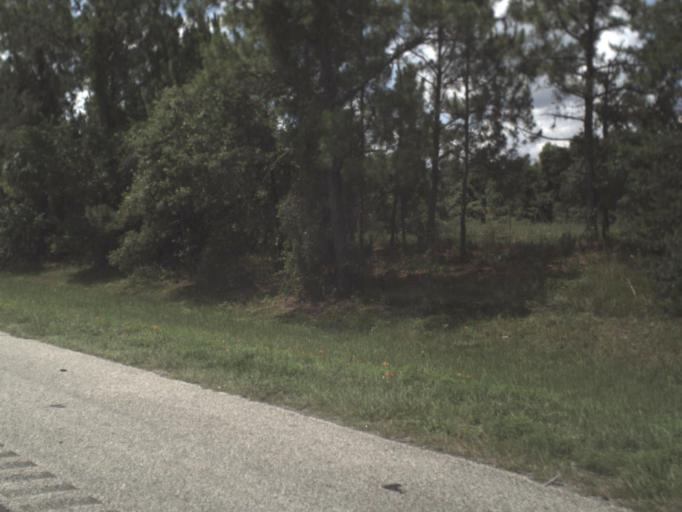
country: US
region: Florida
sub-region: Flagler County
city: Palm Coast
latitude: 29.6565
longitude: -81.2795
